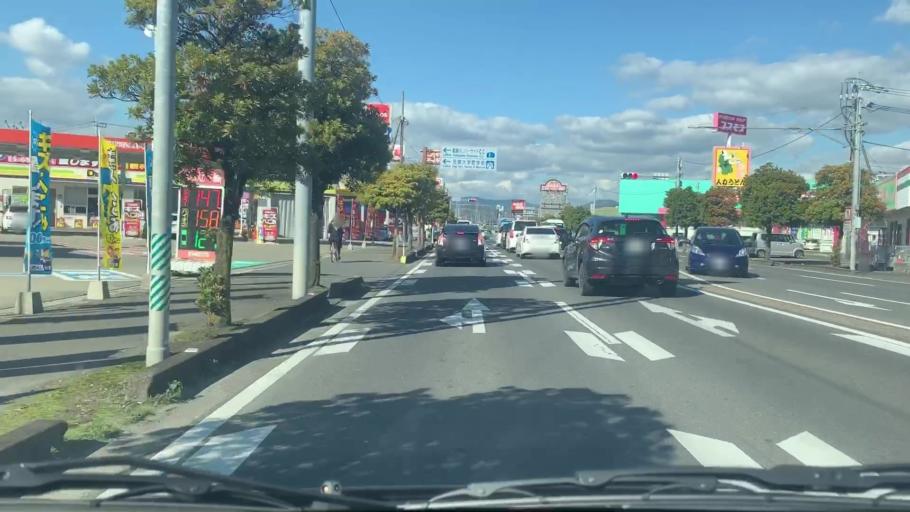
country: JP
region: Saga Prefecture
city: Saga-shi
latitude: 33.2910
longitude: 130.2864
